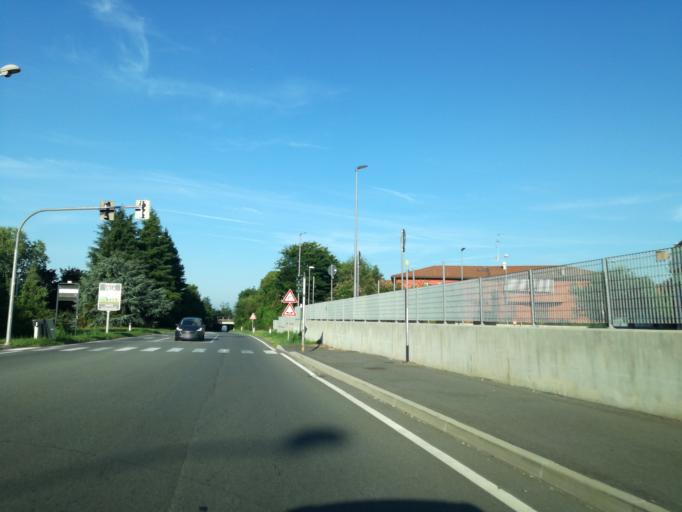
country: IT
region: Lombardy
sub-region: Provincia di Monza e Brianza
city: Carnate
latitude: 45.6453
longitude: 9.3796
